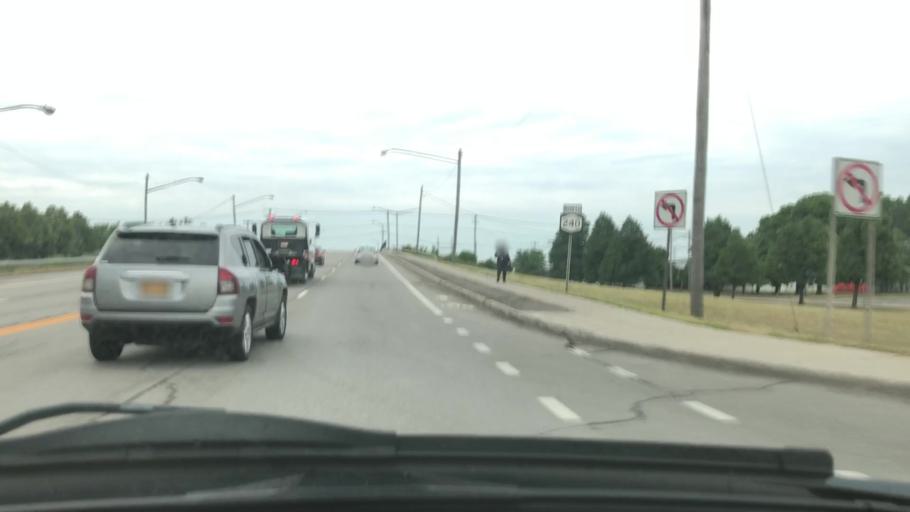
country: US
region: New York
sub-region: Erie County
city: Sloan
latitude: 42.8985
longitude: -78.7841
